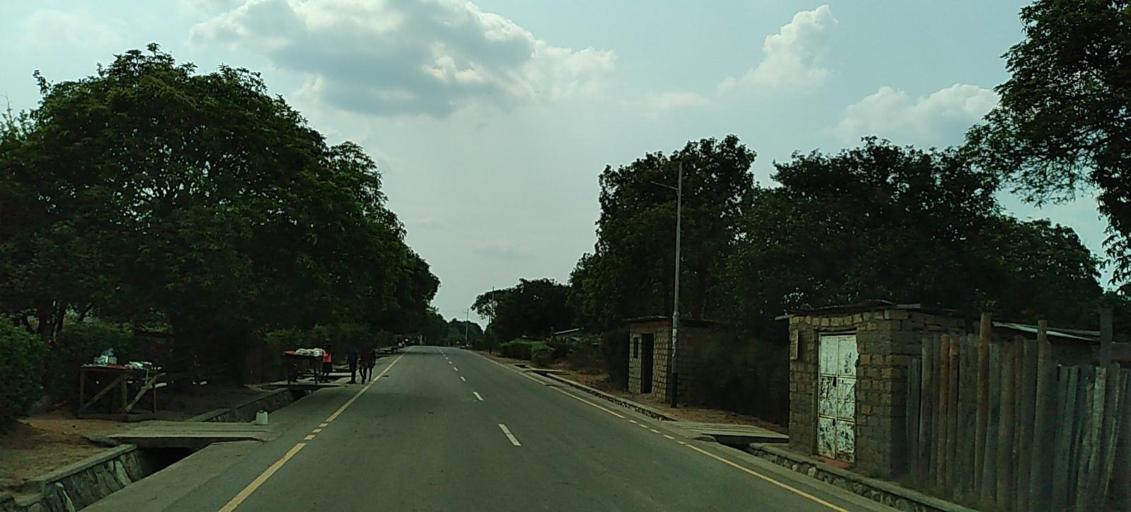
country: ZM
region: Copperbelt
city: Kalulushi
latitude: -12.8573
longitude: 28.1341
